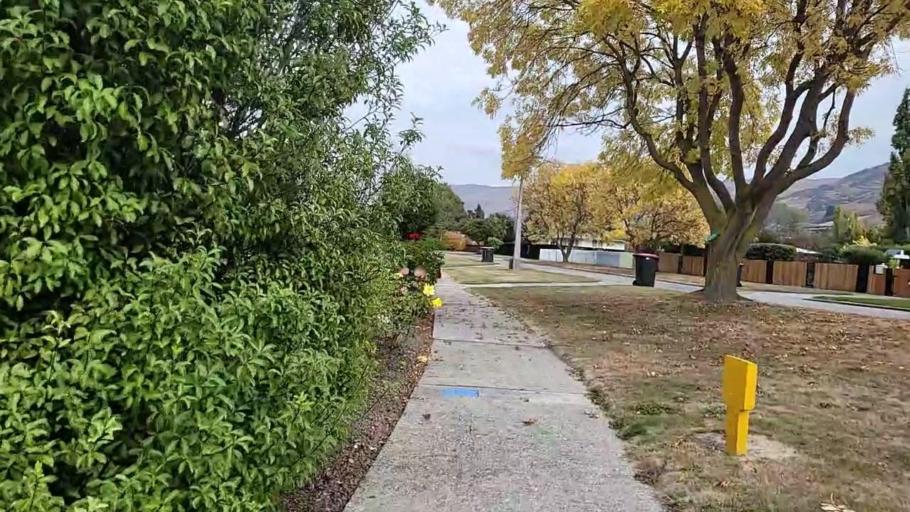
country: NZ
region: Otago
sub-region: Queenstown-Lakes District
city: Kingston
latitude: -45.4787
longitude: 169.3132
